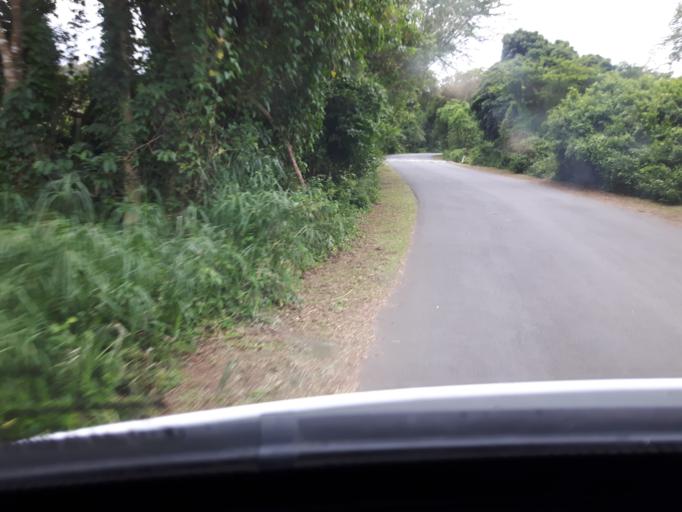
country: ZA
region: KwaZulu-Natal
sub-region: uMkhanyakude District Municipality
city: Mtubatuba
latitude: -28.3862
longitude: 32.4128
